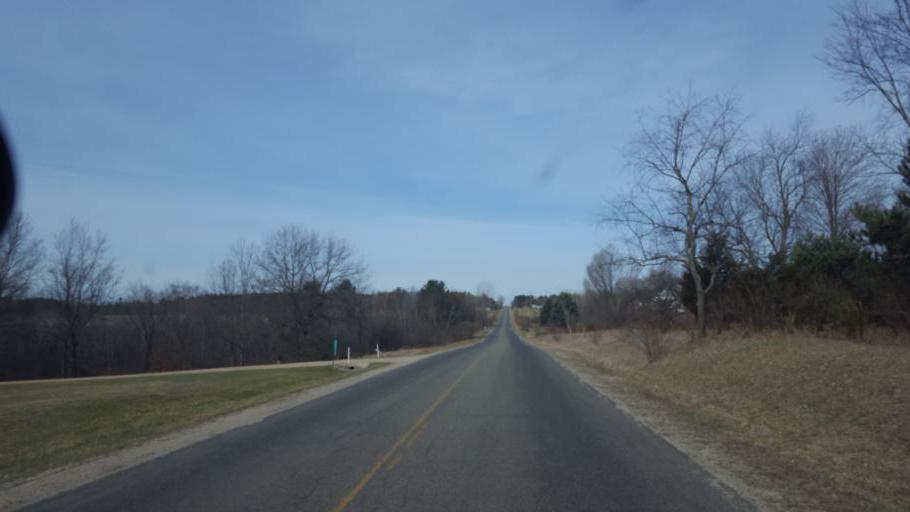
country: US
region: Michigan
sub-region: Montcalm County
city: Howard City
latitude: 43.5261
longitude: -85.4672
